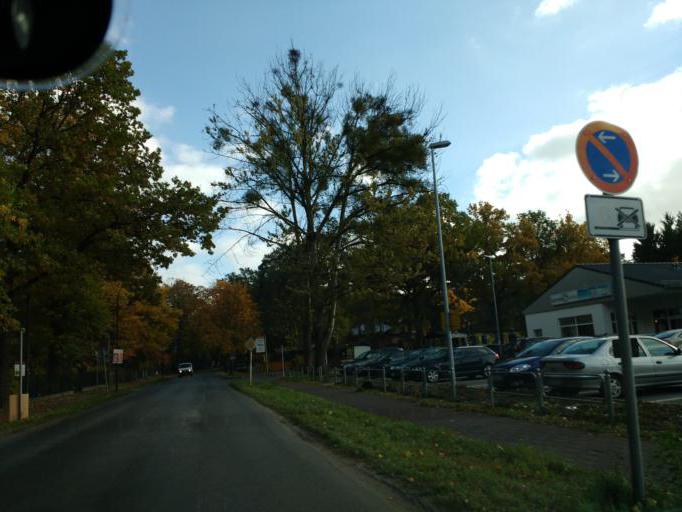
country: DE
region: Brandenburg
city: Petershagen
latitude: 52.5564
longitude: 13.8297
